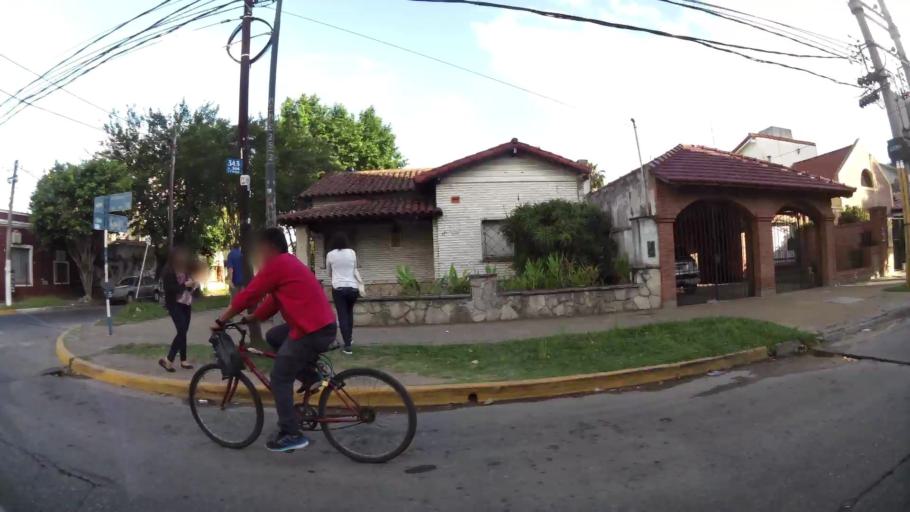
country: AR
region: Buenos Aires
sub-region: Partido de General San Martin
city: General San Martin
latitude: -34.5503
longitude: -58.5498
